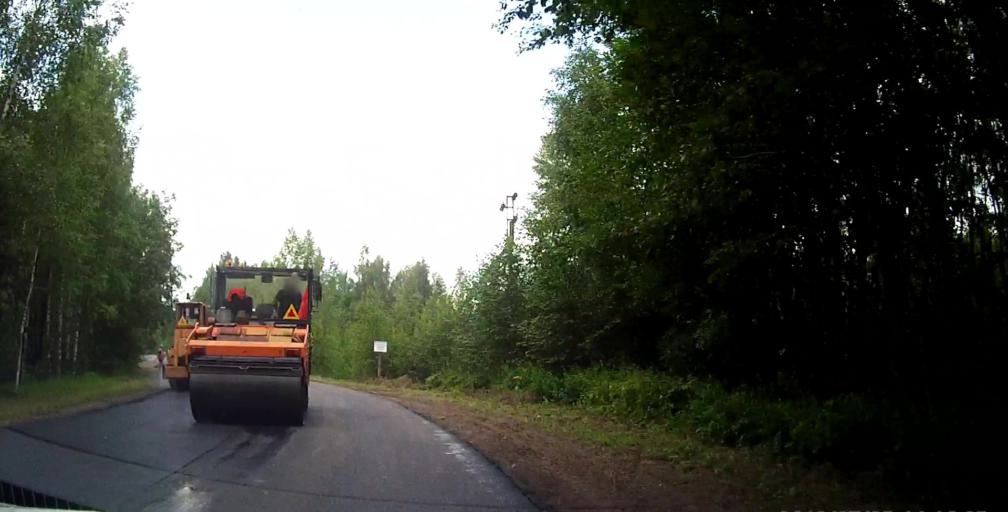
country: RU
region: Smolensk
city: Demidov
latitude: 55.4891
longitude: 31.6372
